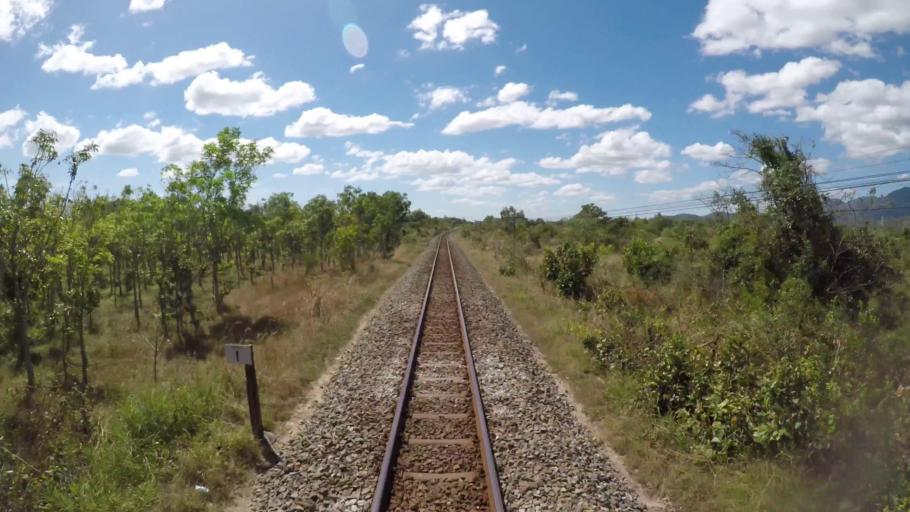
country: VN
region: Binh Thuan
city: Ma Lam
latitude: 11.0317
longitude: 108.0747
